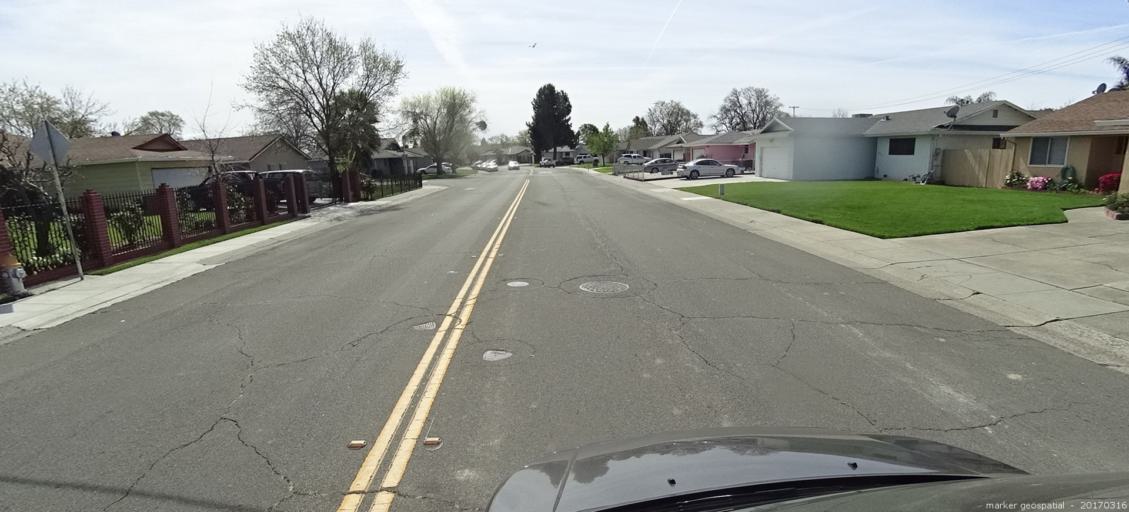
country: US
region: California
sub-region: Sacramento County
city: Parkway
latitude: 38.4862
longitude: -121.5049
